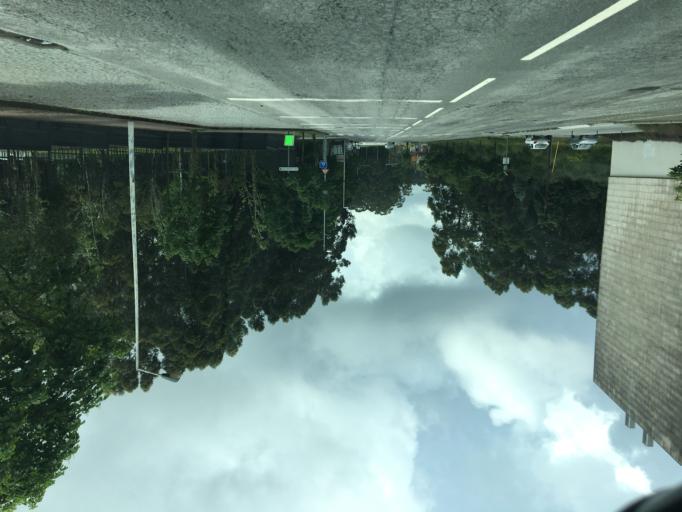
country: PT
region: Porto
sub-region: Maia
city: Anta
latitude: 41.2599
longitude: -8.6108
